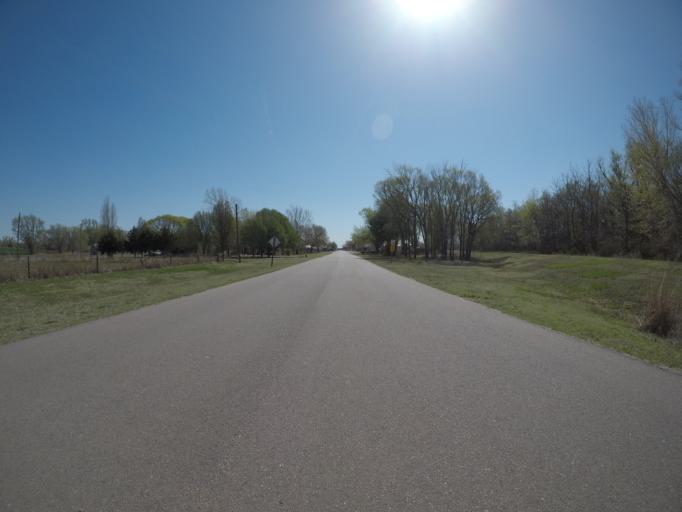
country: US
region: Kansas
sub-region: Pratt County
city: Pratt
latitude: 37.3791
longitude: -98.9200
